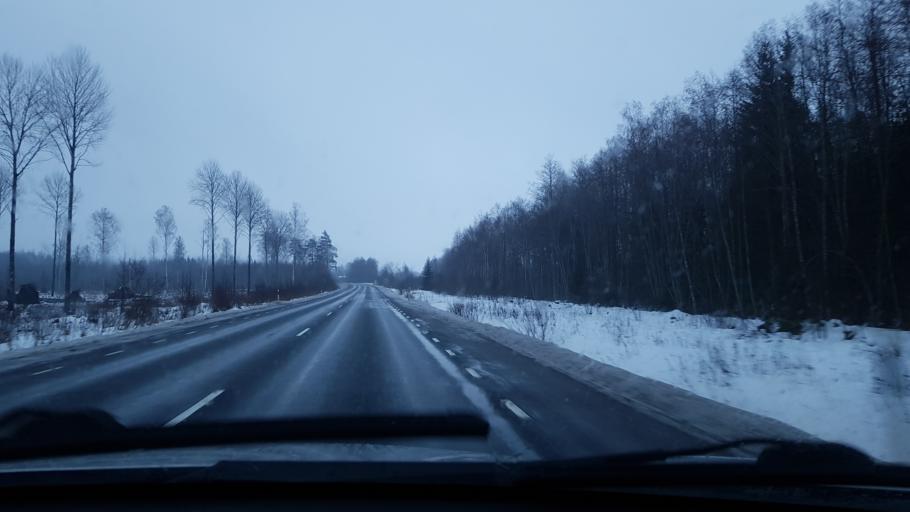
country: EE
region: Jaervamaa
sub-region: Tueri vald
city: Sarevere
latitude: 58.8018
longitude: 25.2296
